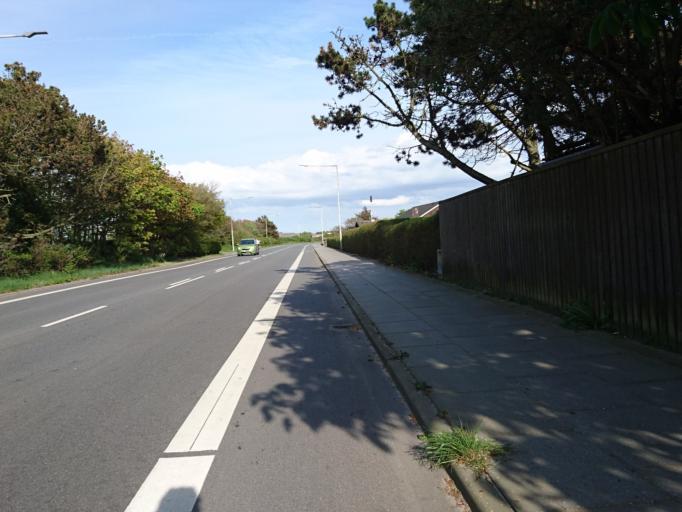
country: DK
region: North Denmark
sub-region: Frederikshavn Kommune
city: Skagen
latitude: 57.7293
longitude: 10.5522
